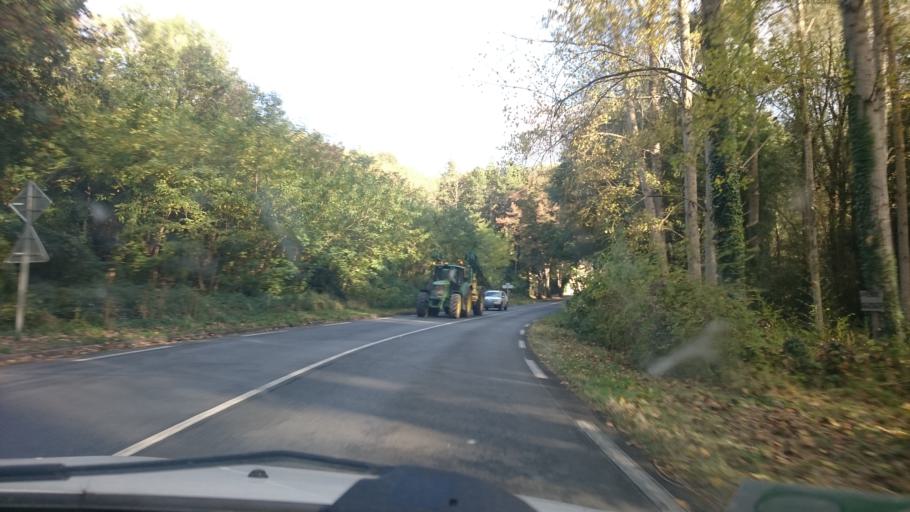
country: FR
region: Centre
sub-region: Departement de l'Indre
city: Saint-Marcel
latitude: 46.6318
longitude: 1.4732
